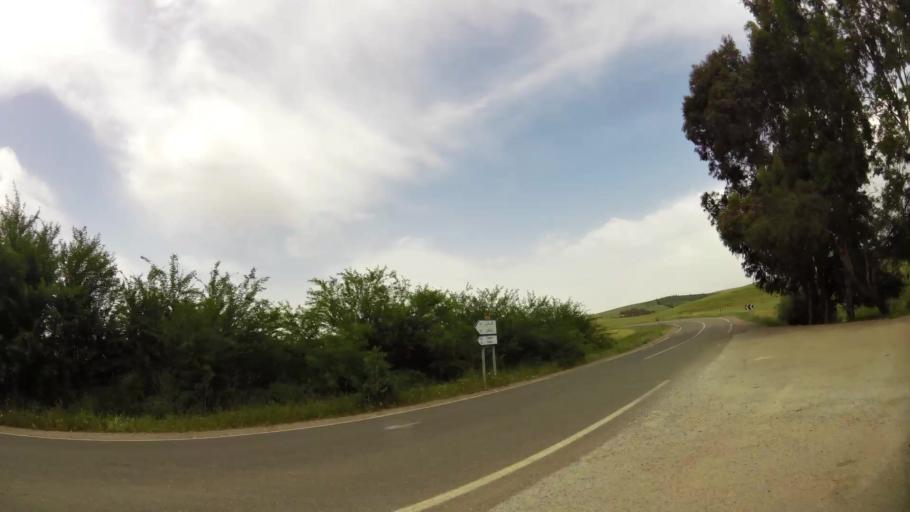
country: MA
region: Rabat-Sale-Zemmour-Zaer
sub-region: Khemisset
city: Khemisset
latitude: 33.7527
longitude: -6.1977
